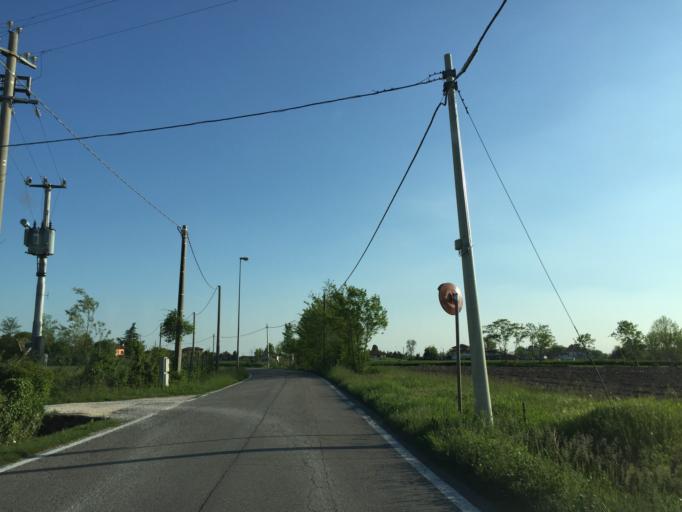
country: IT
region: Friuli Venezia Giulia
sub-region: Provincia di Pordenone
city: Vigonovo-Fontanafredda
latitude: 45.9641
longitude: 12.5727
